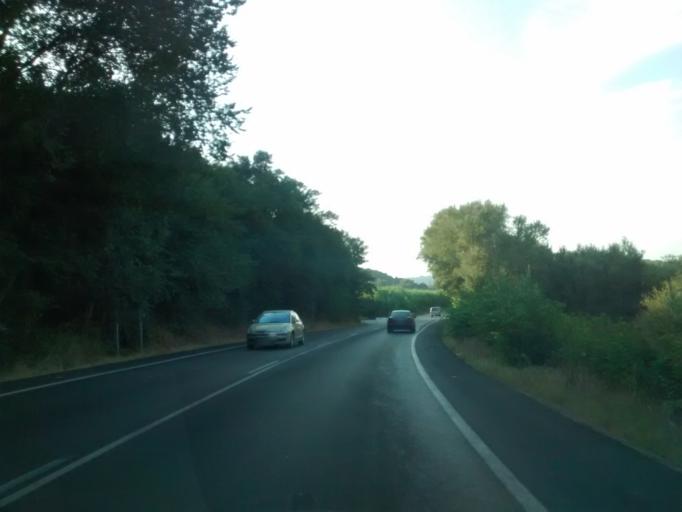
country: ES
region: Andalusia
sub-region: Provincia de Cadiz
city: Vejer de la Frontera
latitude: 36.2560
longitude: -5.9592
